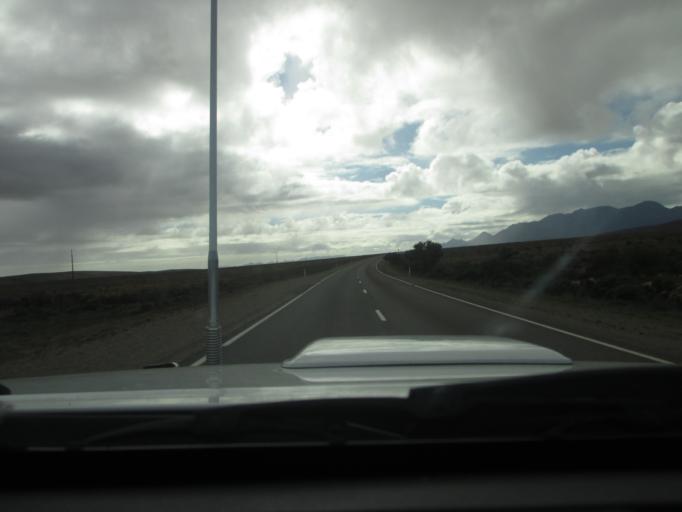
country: AU
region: South Australia
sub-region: Flinders Ranges
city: Quorn
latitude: -31.6008
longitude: 138.4028
